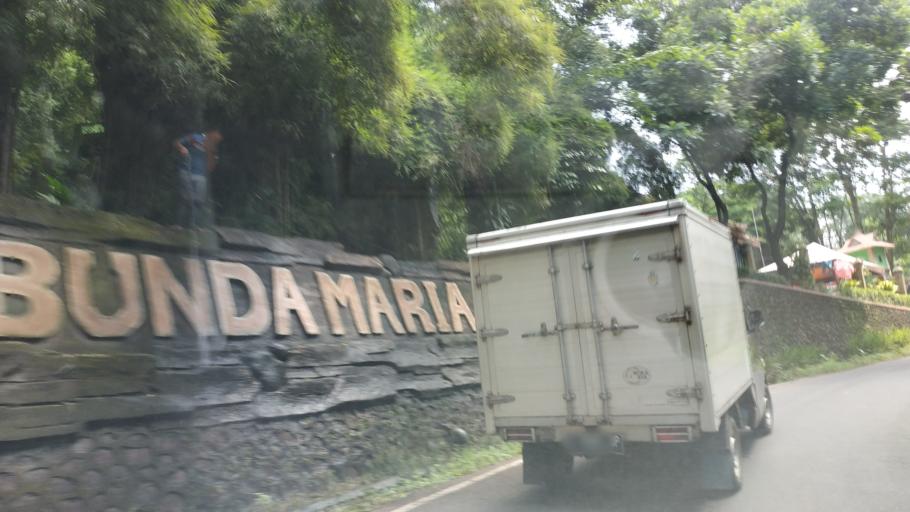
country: ID
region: Central Java
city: Weleri
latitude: -7.0029
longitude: 110.0660
